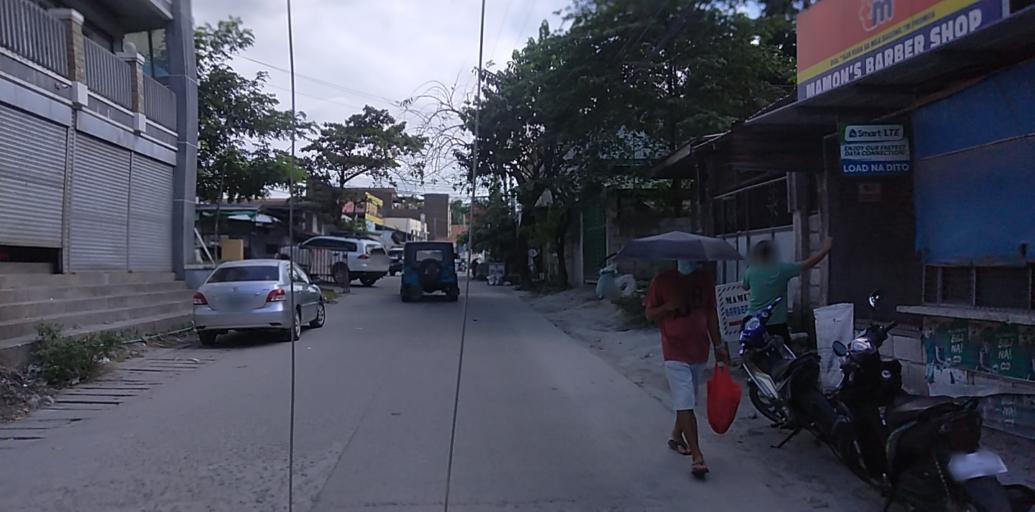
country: PH
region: Central Luzon
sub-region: Province of Pampanga
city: Porac
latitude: 15.0696
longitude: 120.5434
